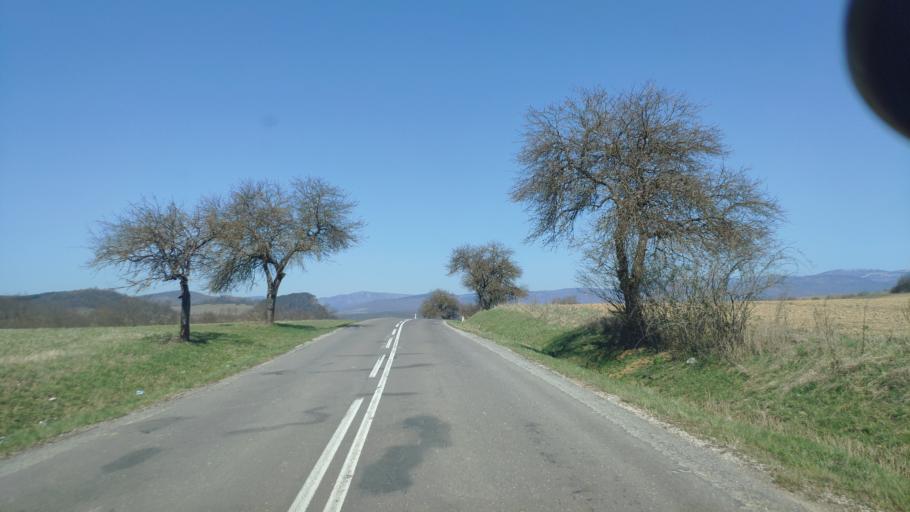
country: SK
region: Kosicky
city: Moldava nad Bodvou
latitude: 48.6652
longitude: 20.9966
